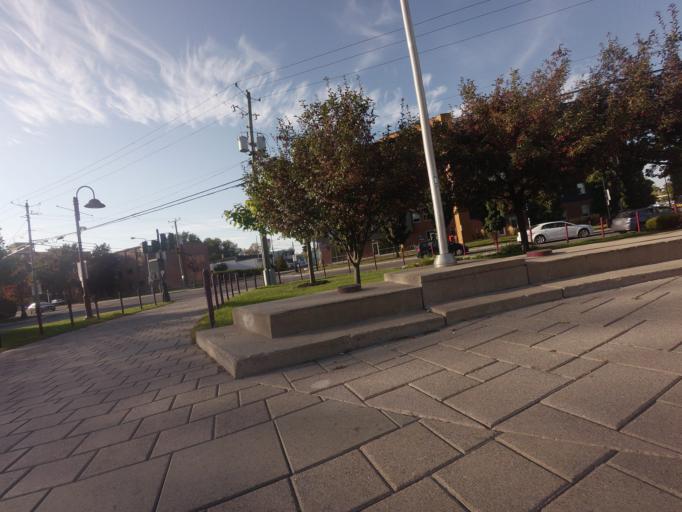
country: CA
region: Quebec
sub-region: Laurentides
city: Saint-Jerome
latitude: 45.7738
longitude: -74.0000
